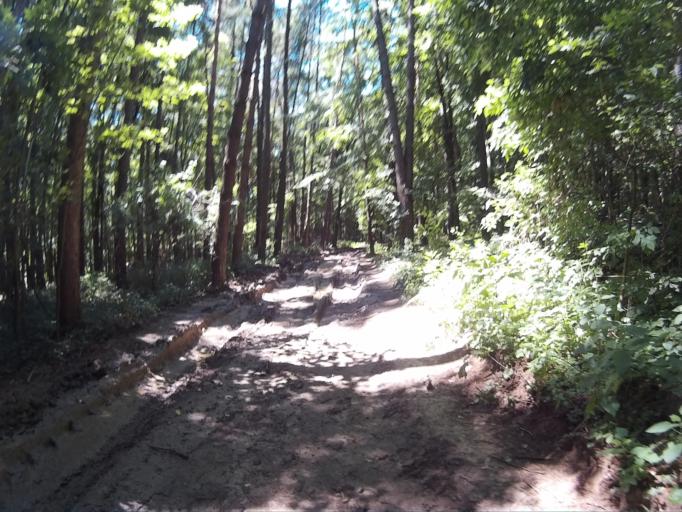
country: HU
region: Veszprem
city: Urkut
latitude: 47.1303
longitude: 17.6477
